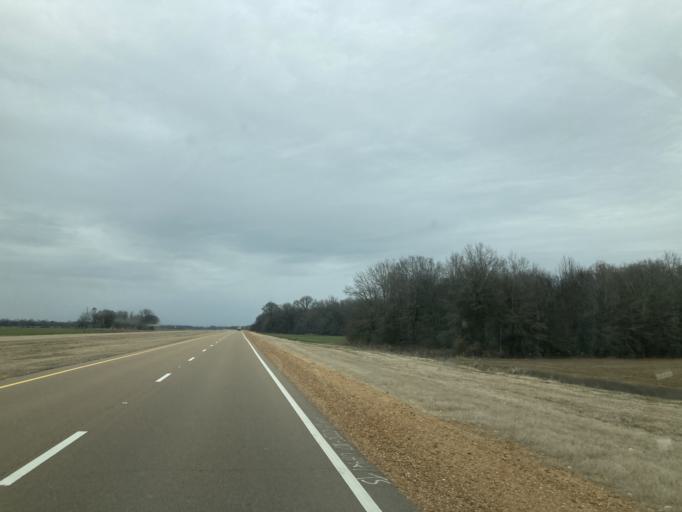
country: US
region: Mississippi
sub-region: Yazoo County
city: Yazoo City
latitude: 33.0050
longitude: -90.4699
